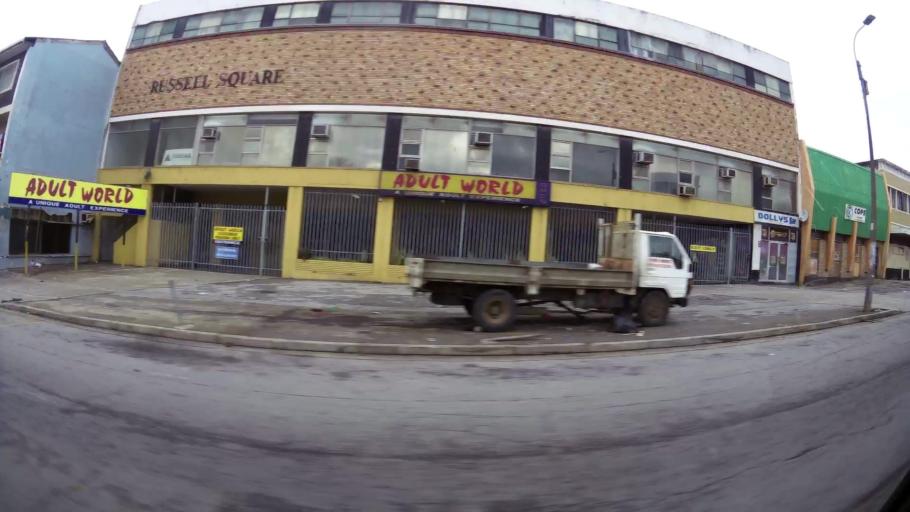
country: ZA
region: Eastern Cape
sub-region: Nelson Mandela Bay Metropolitan Municipality
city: Port Elizabeth
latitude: -33.9616
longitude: 25.6123
